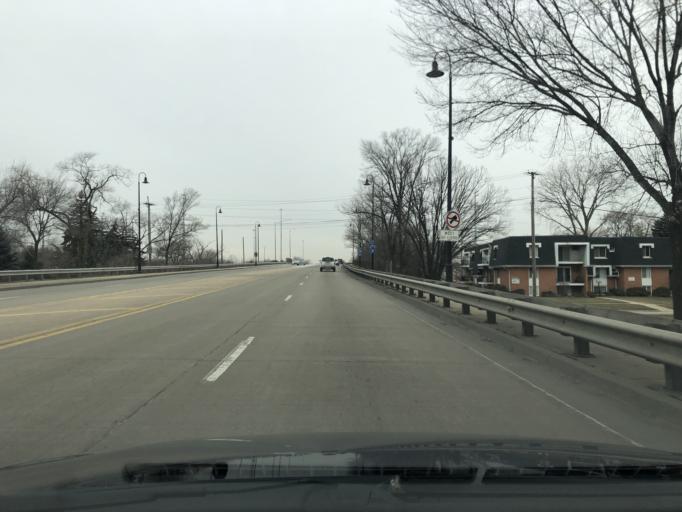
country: US
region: Illinois
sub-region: Cook County
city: Berkeley
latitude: 41.8897
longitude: -87.9147
